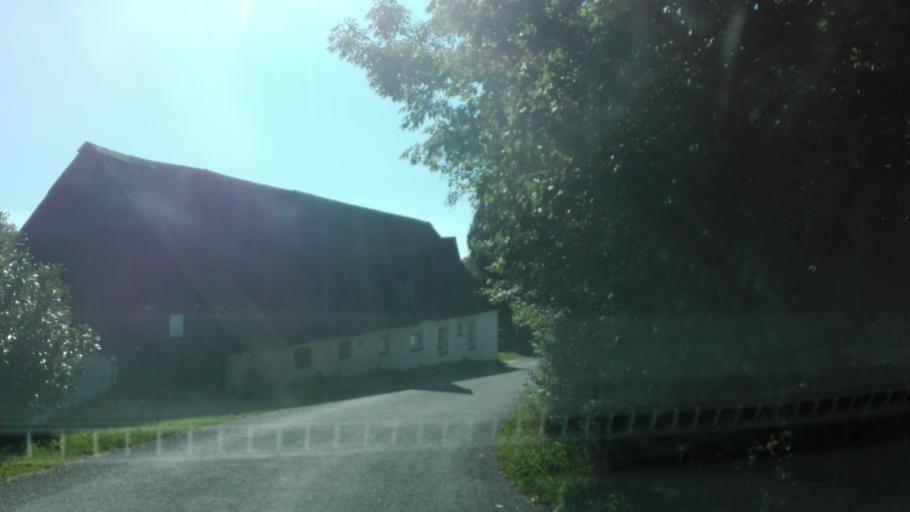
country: DK
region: Central Jutland
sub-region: Syddjurs Kommune
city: Ebeltoft
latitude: 56.2395
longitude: 10.6318
